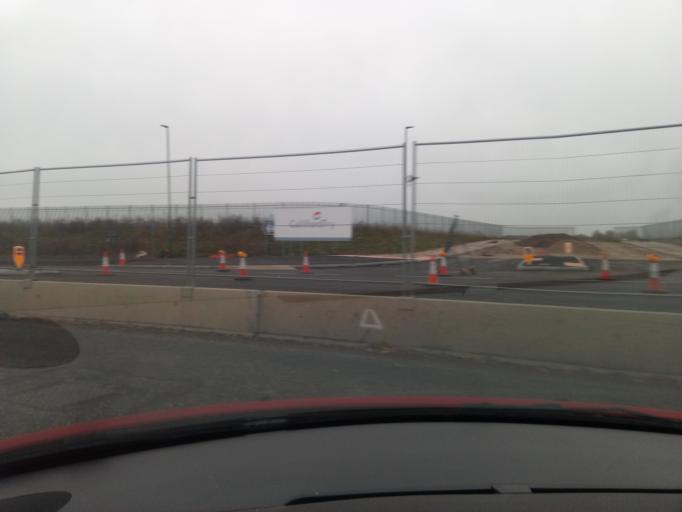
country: GB
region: England
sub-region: Derby
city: Derby
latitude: 52.9172
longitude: -1.4382
